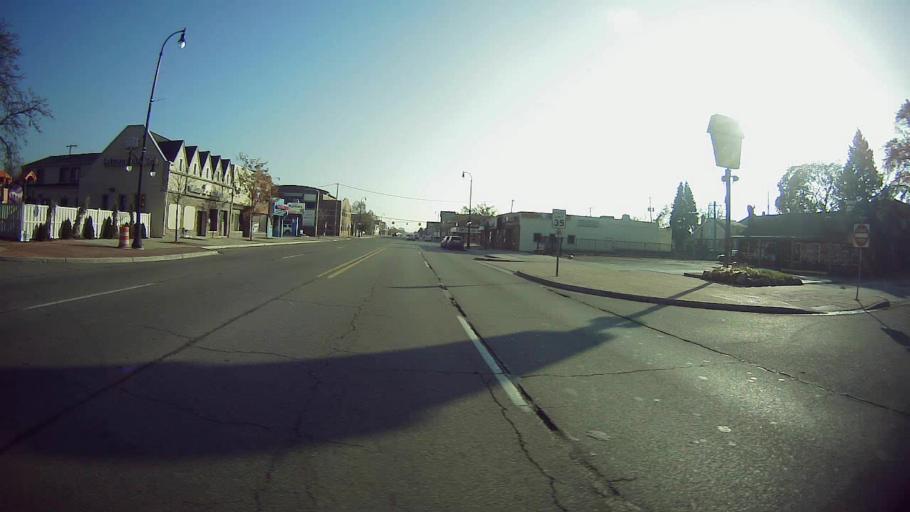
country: US
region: Michigan
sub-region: Wayne County
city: Dearborn
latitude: 42.3441
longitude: -83.1693
